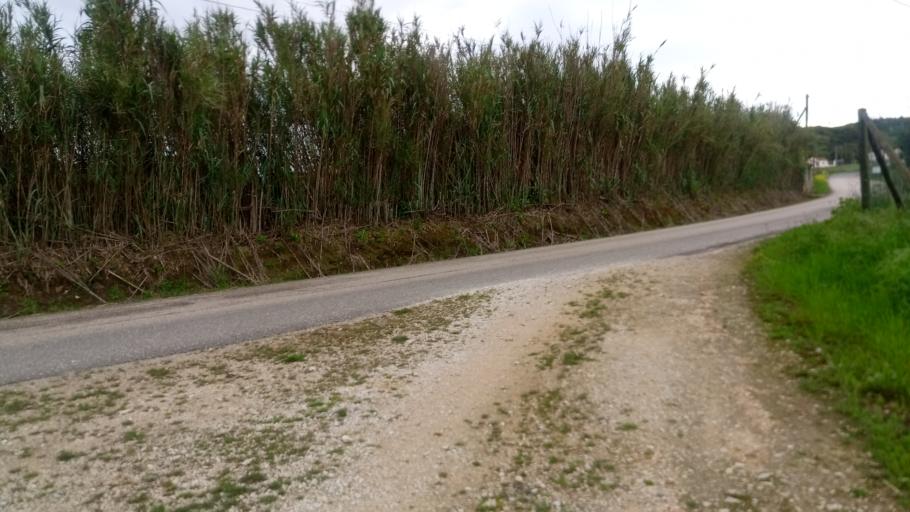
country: PT
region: Leiria
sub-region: Caldas da Rainha
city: Caldas da Rainha
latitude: 39.4540
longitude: -9.1842
